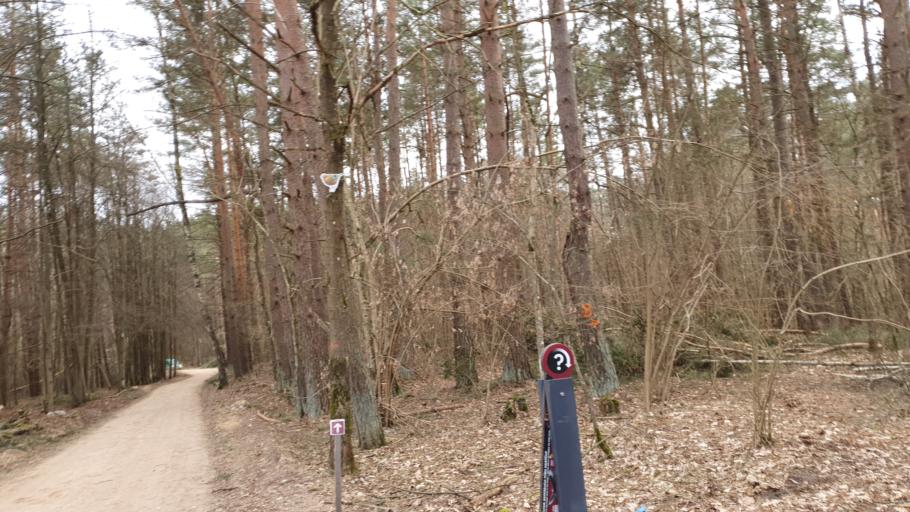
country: LT
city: Grigiskes
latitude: 54.7324
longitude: 25.0279
